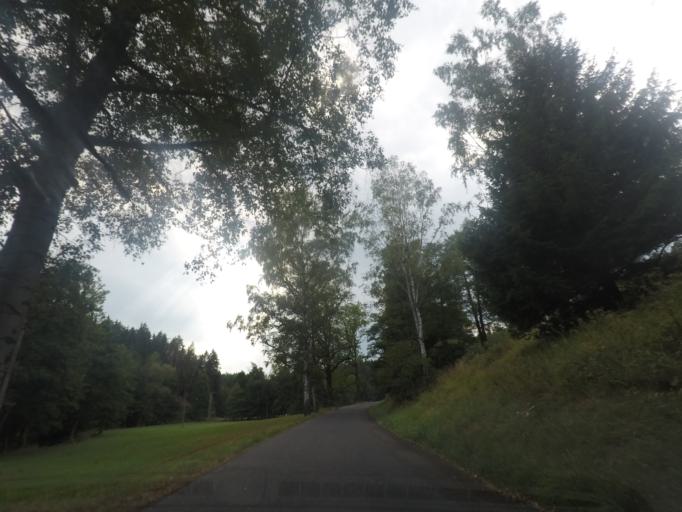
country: CZ
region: Ustecky
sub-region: Okres Decin
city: Chribska
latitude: 50.8613
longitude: 14.4479
